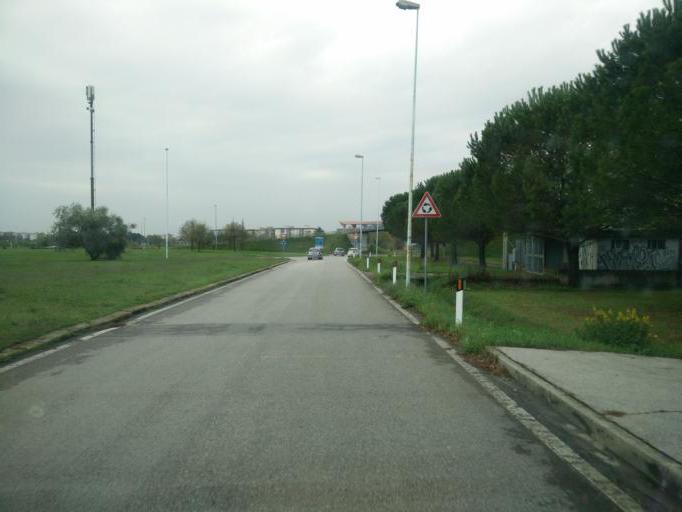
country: IT
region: Tuscany
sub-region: Provincia di Prato
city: Prato
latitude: 43.9035
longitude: 11.0921
